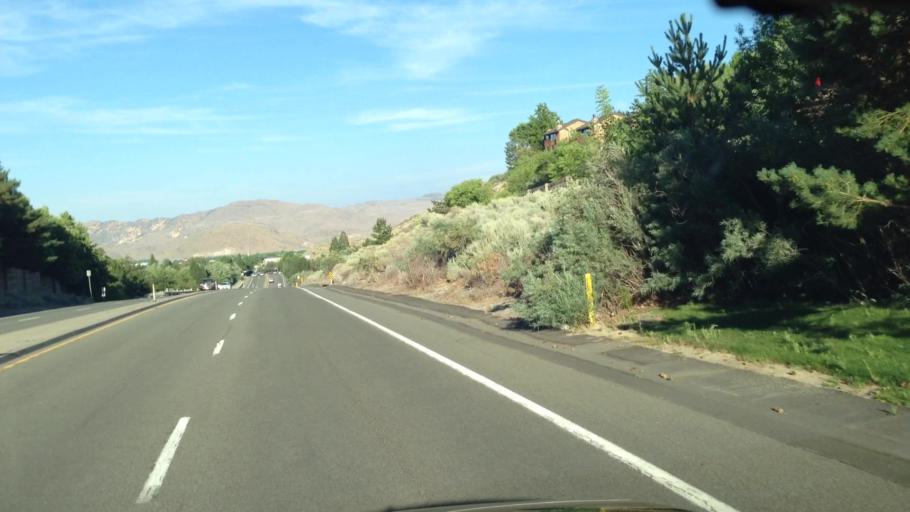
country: US
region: Nevada
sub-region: Washoe County
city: Reno
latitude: 39.4776
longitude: -119.8213
